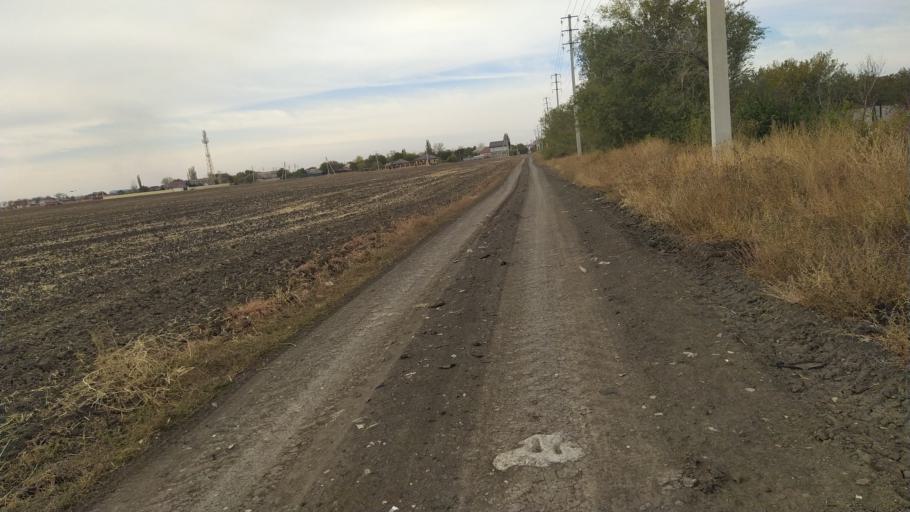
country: RU
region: Rostov
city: Bataysk
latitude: 47.1103
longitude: 39.6824
